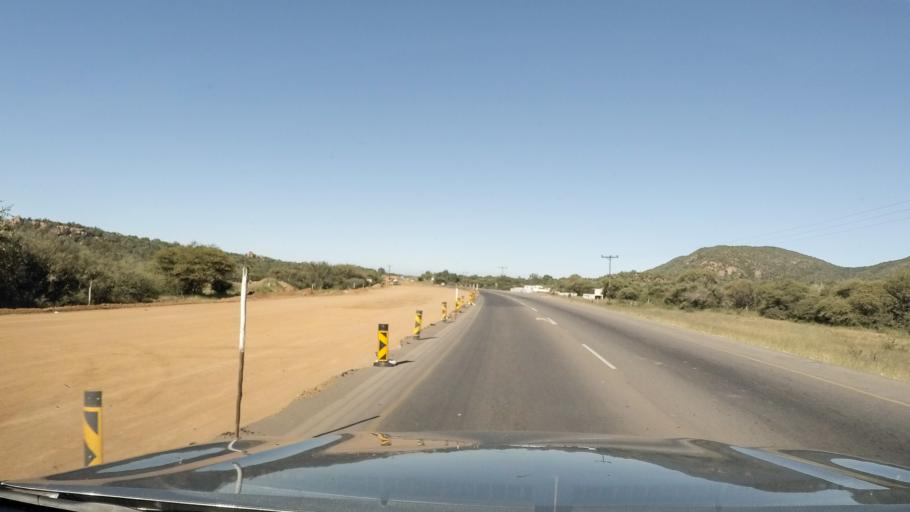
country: BW
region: South East
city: Gaborone
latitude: -24.7031
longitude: 25.8680
